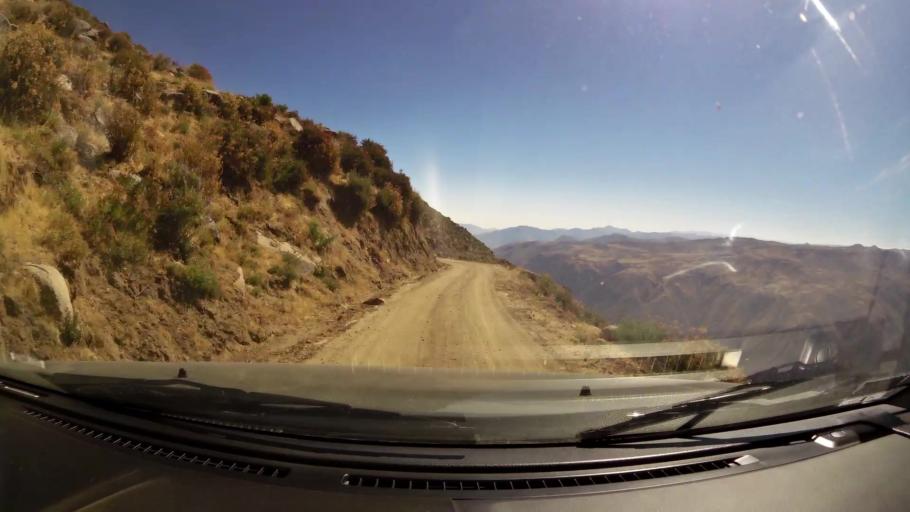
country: PE
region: Huancavelica
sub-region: Huaytara
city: Quito-Arma
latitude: -13.6246
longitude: -75.3489
